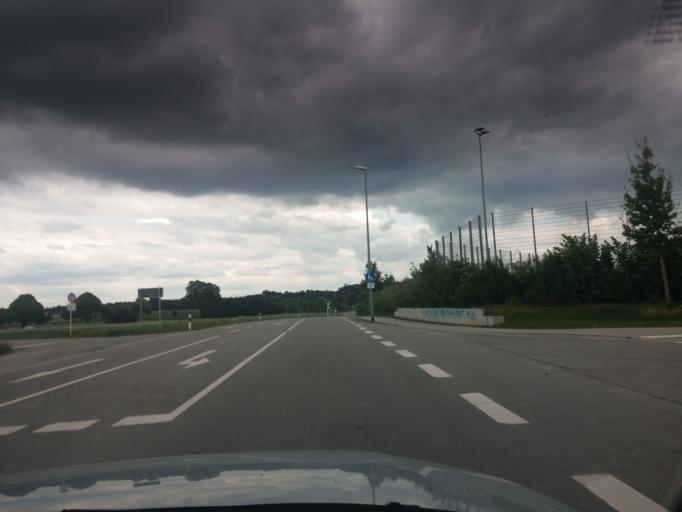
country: DE
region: Bavaria
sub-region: Upper Bavaria
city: Holzkirchen
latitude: 47.8897
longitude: 11.7054
